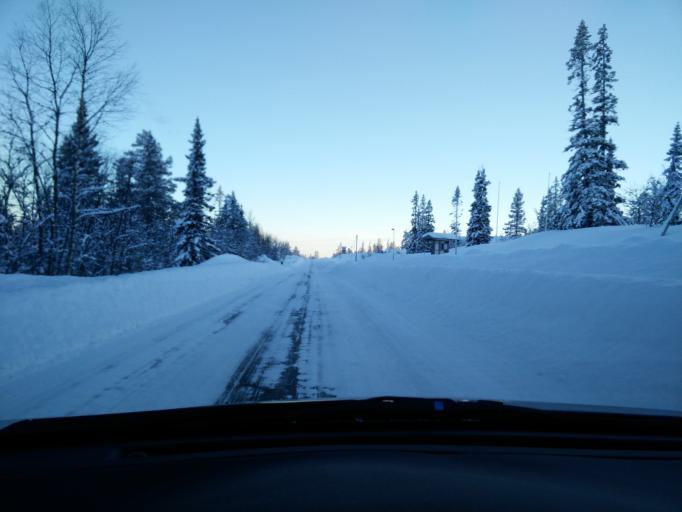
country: SE
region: Jaemtland
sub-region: Bergs Kommun
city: Hoverberg
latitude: 62.4964
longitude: 14.1121
